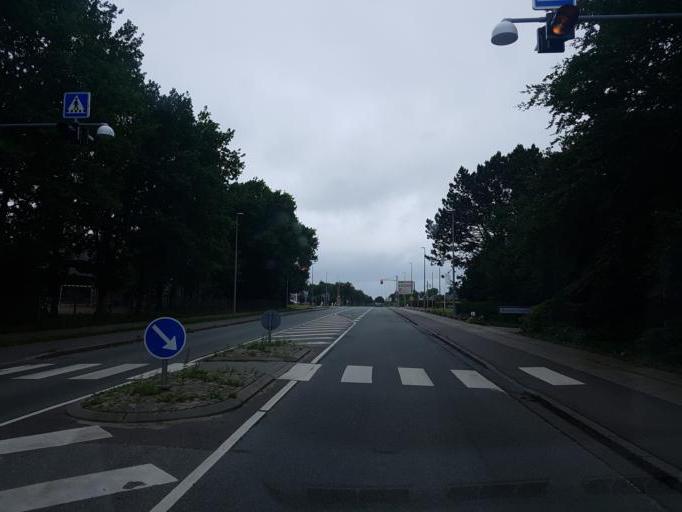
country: DK
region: South Denmark
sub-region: Varde Kommune
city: Varde
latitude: 55.6308
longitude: 8.4841
